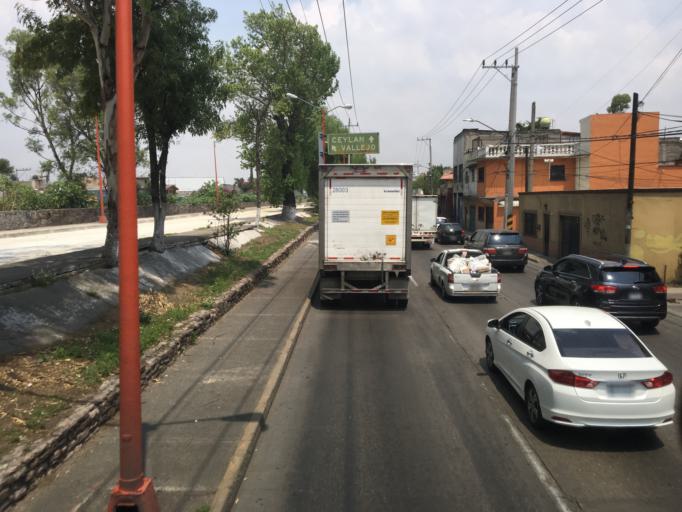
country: MX
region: Mexico
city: Tlalnepantla
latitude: 19.5287
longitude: -99.1648
